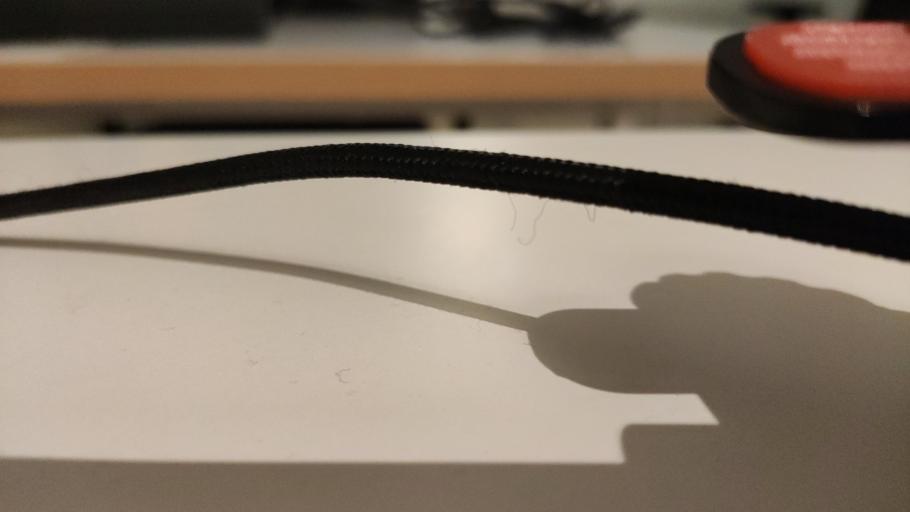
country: RU
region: Moskovskaya
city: Rogachevo
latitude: 56.4390
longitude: 37.1794
